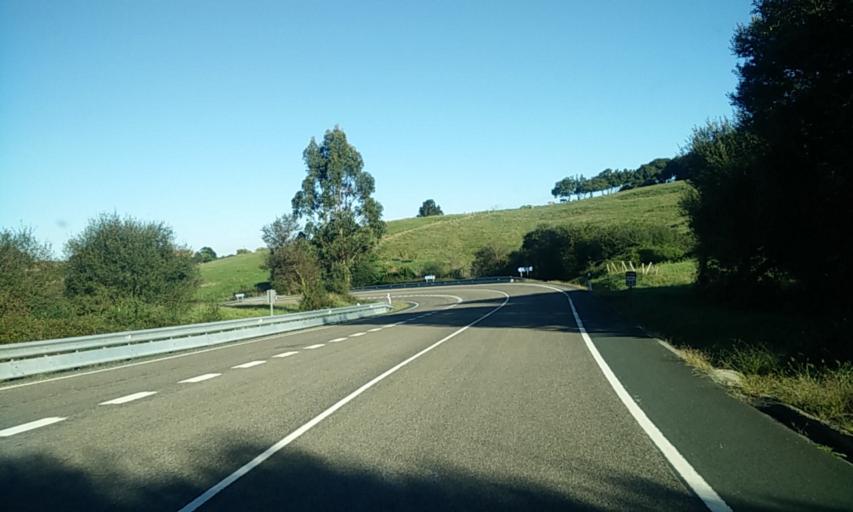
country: ES
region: Cantabria
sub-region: Provincia de Cantabria
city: San Vicente de la Barquera
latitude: 43.3826
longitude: -4.3824
